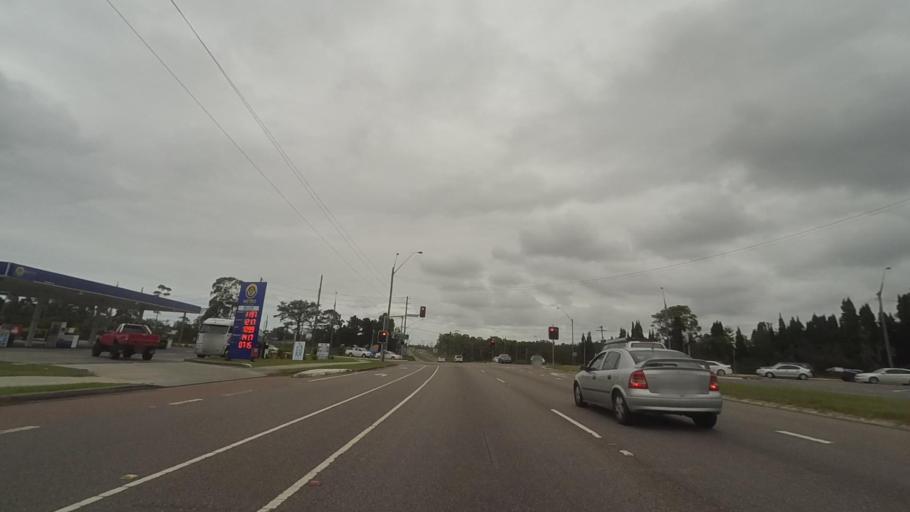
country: AU
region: New South Wales
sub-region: Wyong Shire
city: Buff Point
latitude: -33.1991
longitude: 151.5231
